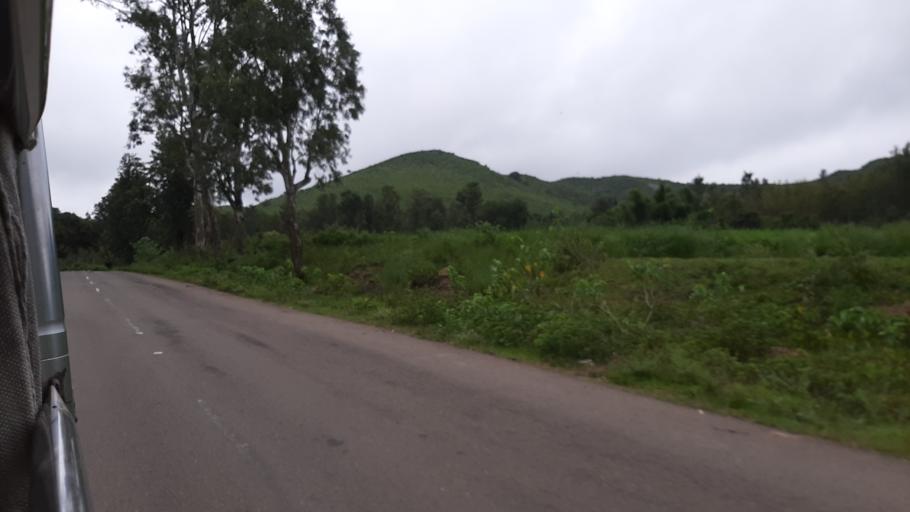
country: IN
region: Andhra Pradesh
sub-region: Vizianagaram District
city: Salur
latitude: 18.2872
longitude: 82.9334
